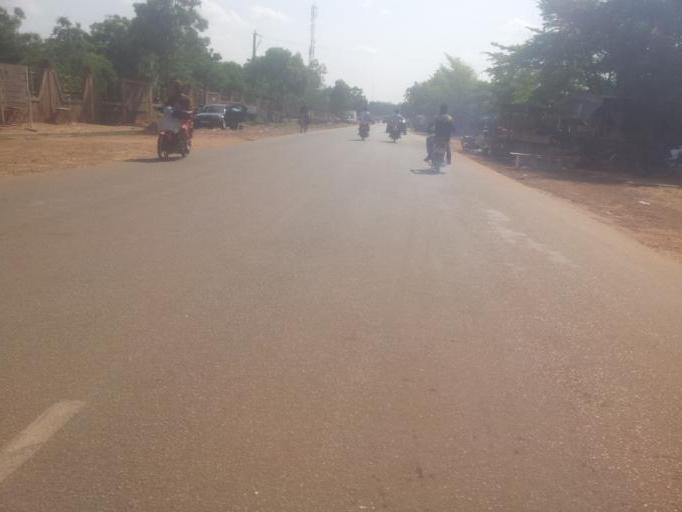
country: BF
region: Centre
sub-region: Kadiogo Province
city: Ouagadougou
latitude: 12.3641
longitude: -1.5559
